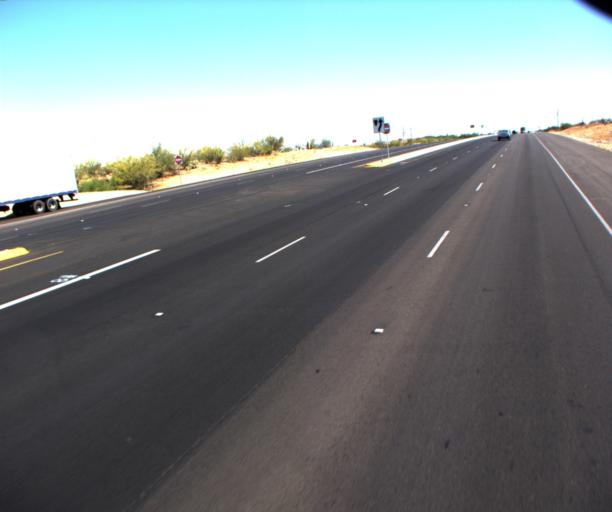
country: US
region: Arizona
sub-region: Pima County
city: Oro Valley
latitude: 32.4346
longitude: -110.9339
